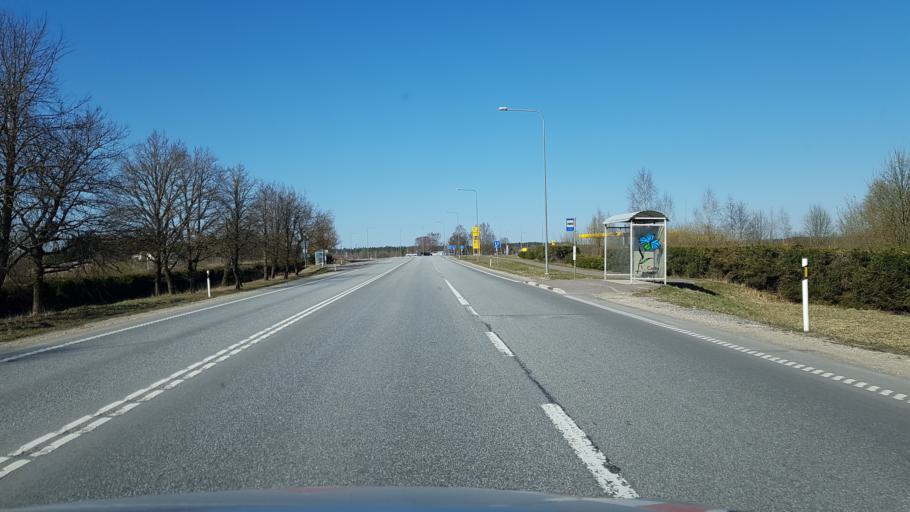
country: EE
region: Tartu
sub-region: Tartu linn
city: Tartu
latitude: 58.4451
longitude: 26.8070
